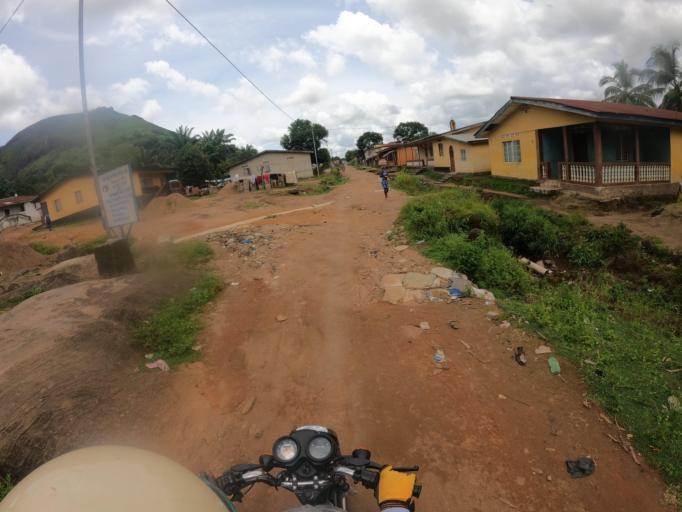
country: SL
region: Northern Province
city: Makeni
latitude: 8.8984
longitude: -12.0458
